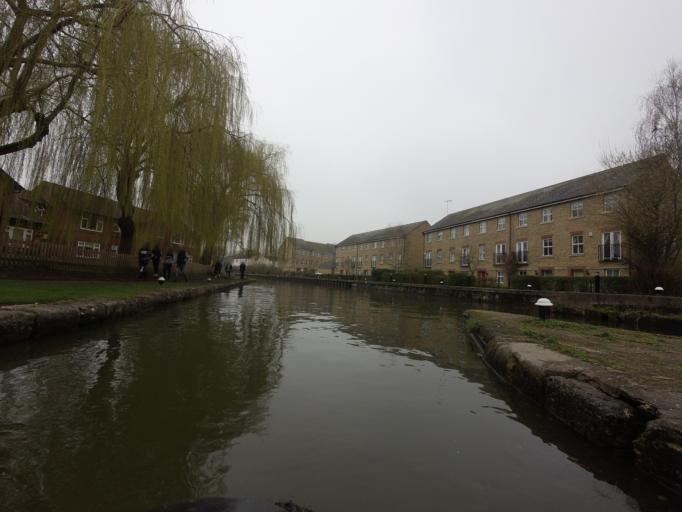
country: GB
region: England
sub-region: Hertfordshire
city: Berkhamsted
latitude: 51.7590
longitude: -0.5562
